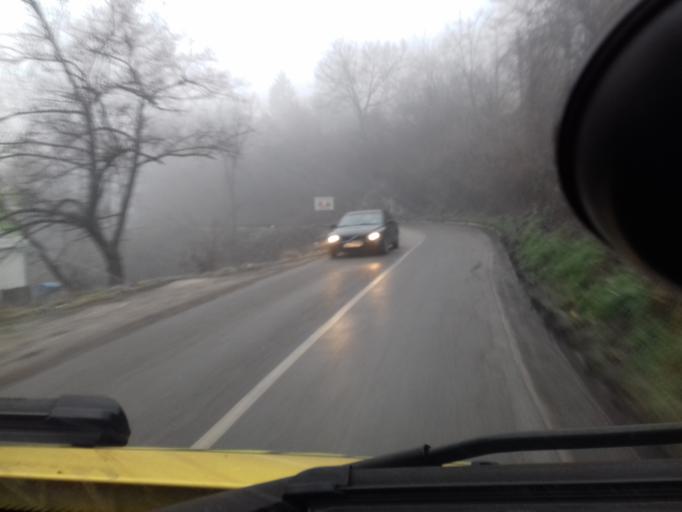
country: BA
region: Federation of Bosnia and Herzegovina
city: Lokvine
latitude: 44.1945
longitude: 17.8759
